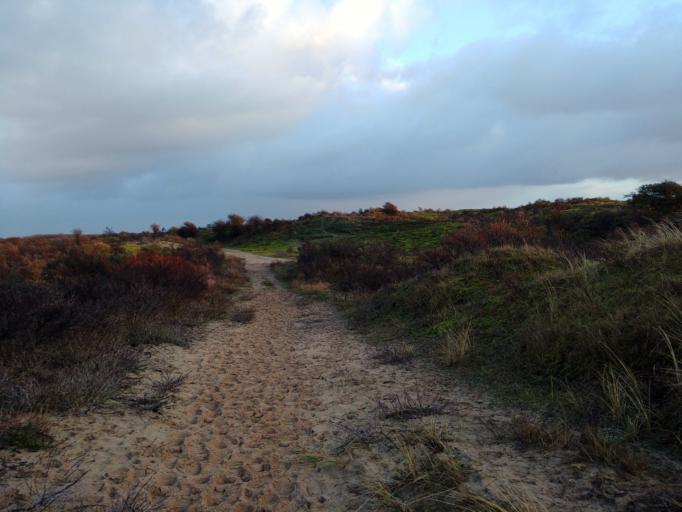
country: NL
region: South Holland
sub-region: Gemeente Noordwijkerhout
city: Noordwijkerhout
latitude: 52.3104
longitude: 4.4934
